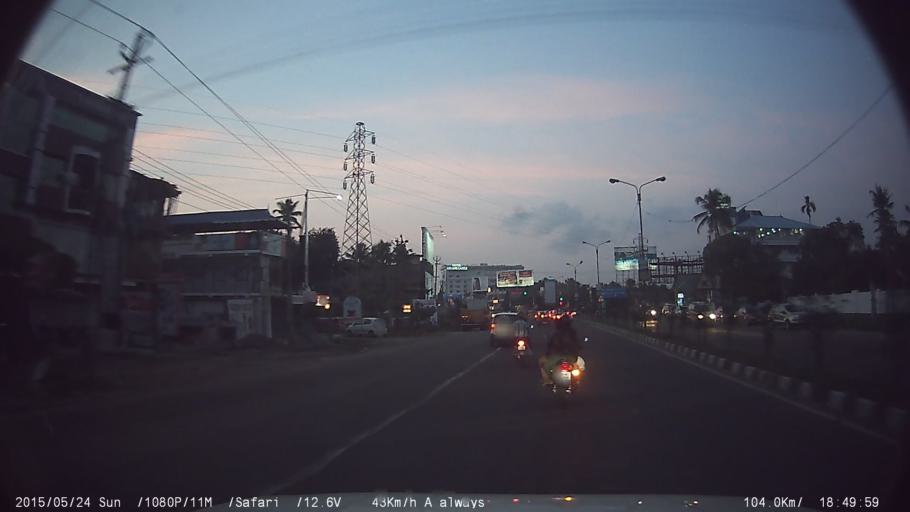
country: IN
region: Kerala
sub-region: Ernakulam
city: Aluva
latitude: 10.1516
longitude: 76.3544
